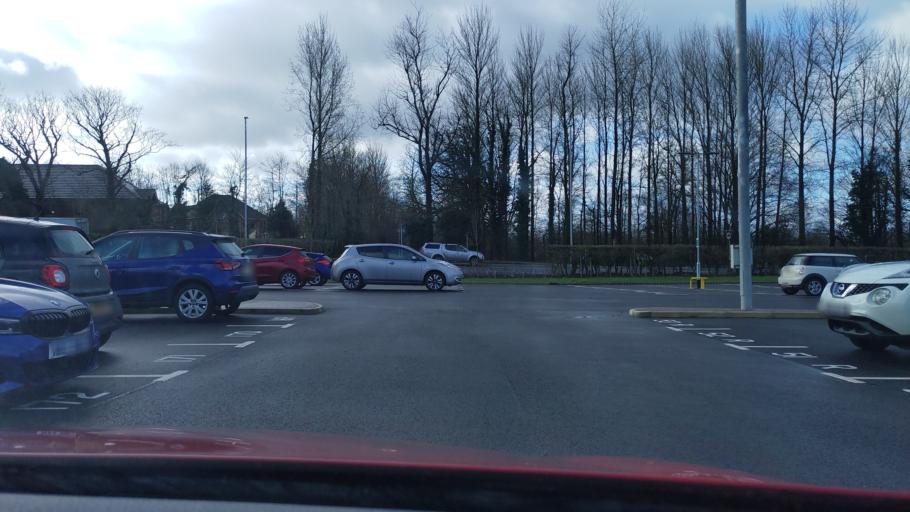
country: GB
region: England
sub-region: Lancashire
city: Chorley
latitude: 53.6679
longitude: -2.6415
